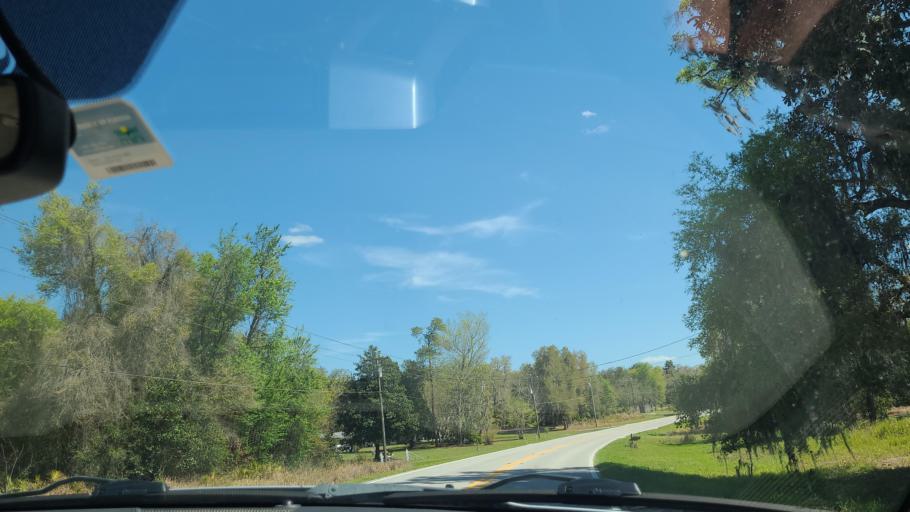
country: US
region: Florida
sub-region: Putnam County
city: Crescent City
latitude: 29.3732
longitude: -81.7443
